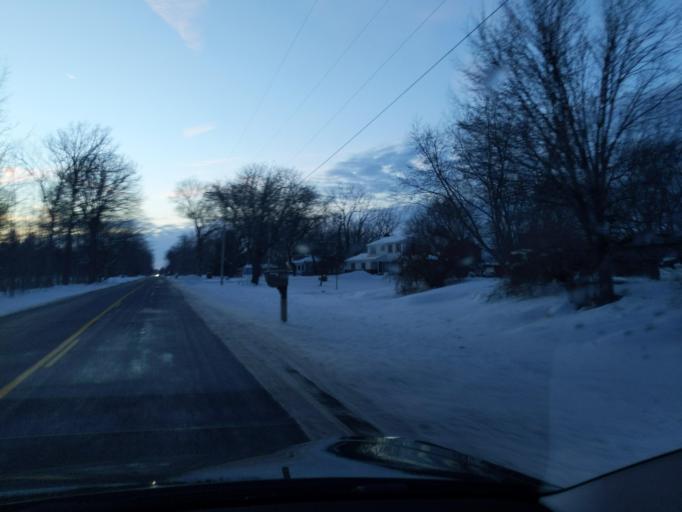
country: US
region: Michigan
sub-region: Ingham County
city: Mason
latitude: 42.5822
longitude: -84.4167
